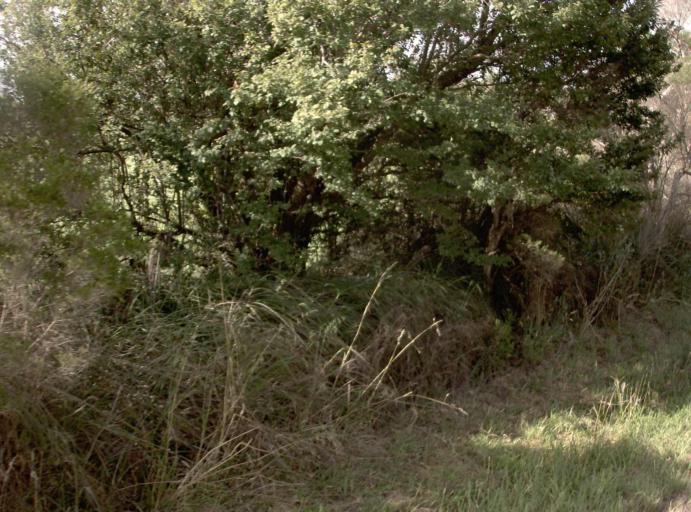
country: AU
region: Victoria
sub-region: Cardinia
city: Bunyip
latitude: -38.1462
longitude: 145.7428
